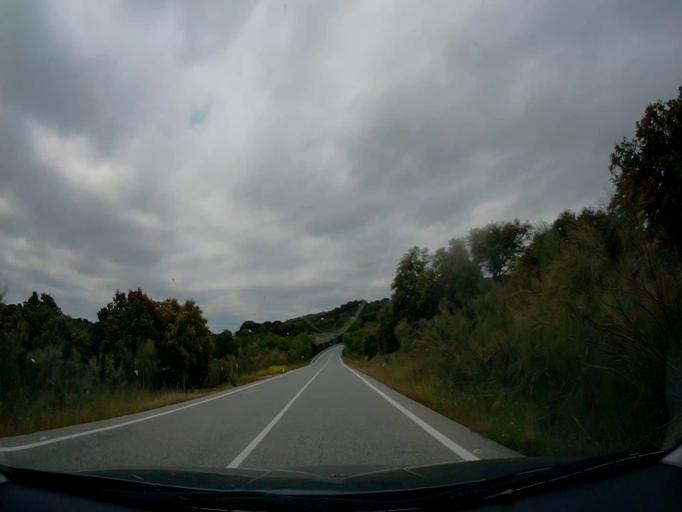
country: ES
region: Madrid
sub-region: Provincia de Madrid
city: Navalagamella
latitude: 40.4308
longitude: -4.1036
